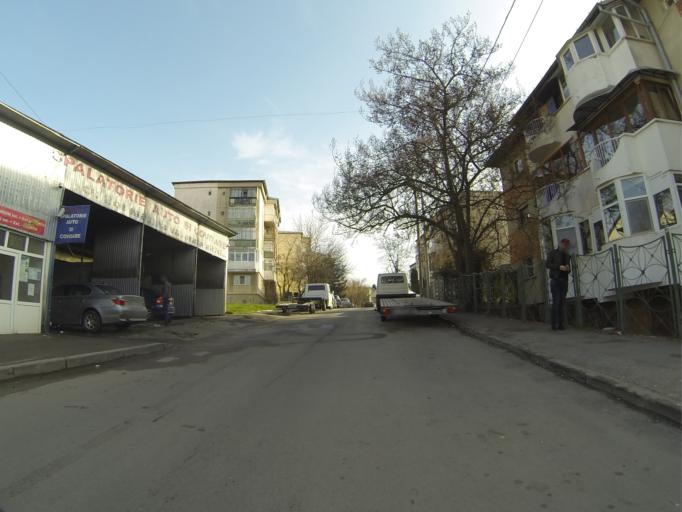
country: RO
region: Dolj
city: Craiova
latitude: 44.3072
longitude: 23.8142
